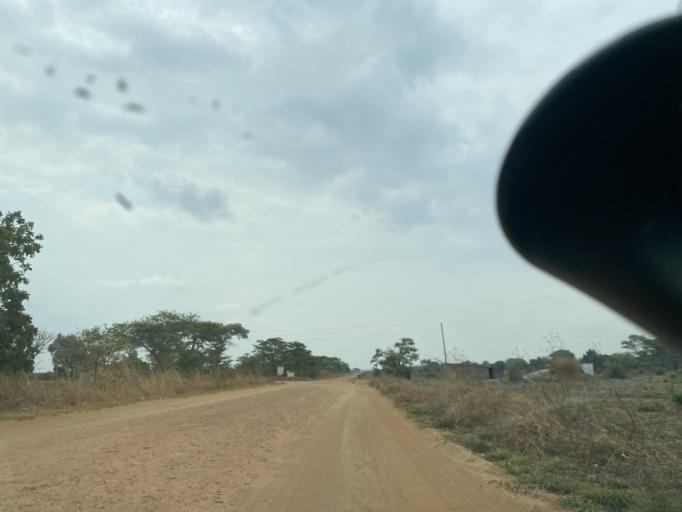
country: ZM
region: Lusaka
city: Lusaka
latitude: -15.2296
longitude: 28.3357
